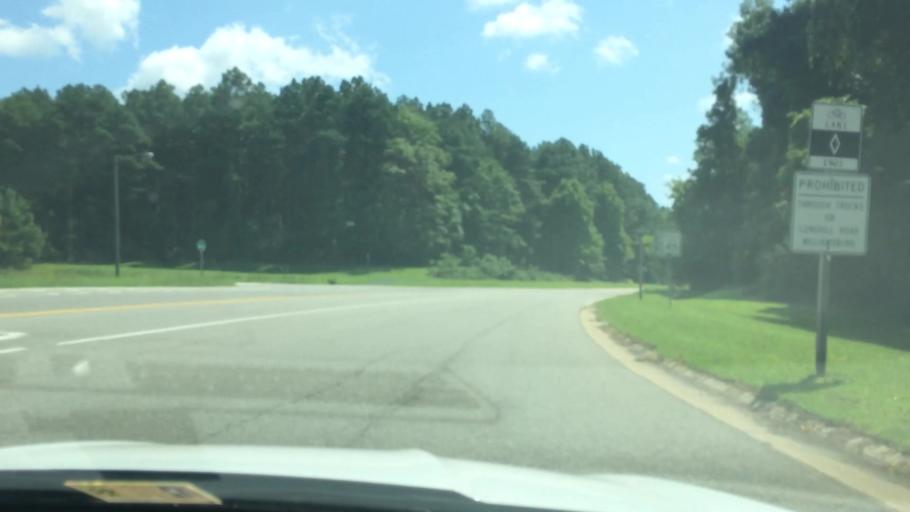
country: US
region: Virginia
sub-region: James City County
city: Williamsburg
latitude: 37.2980
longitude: -76.7415
